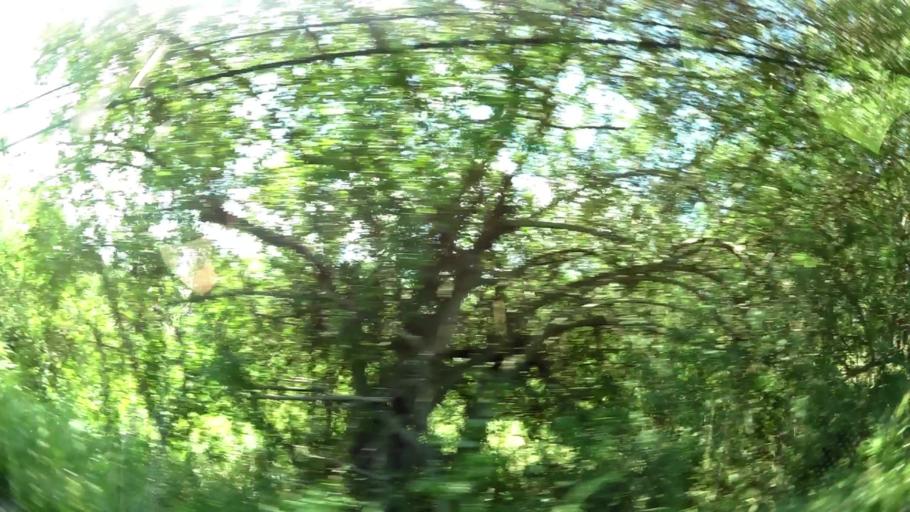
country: GP
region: Guadeloupe
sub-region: Guadeloupe
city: Petit-Canal
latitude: 16.3621
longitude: -61.4288
